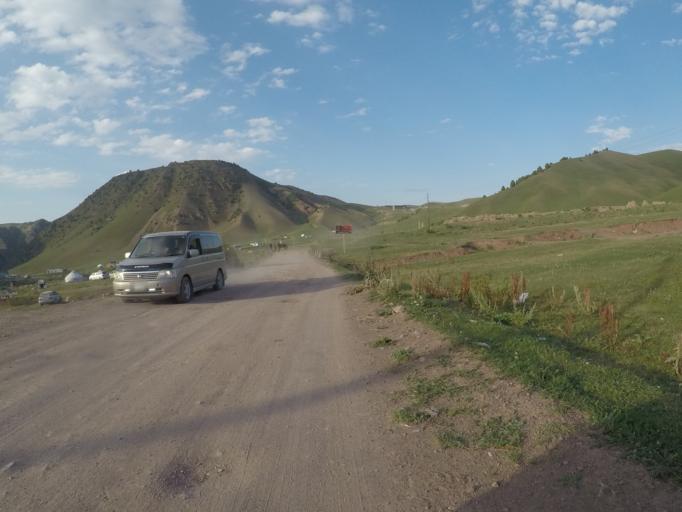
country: KG
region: Chuy
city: Bishkek
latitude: 42.6369
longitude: 74.6185
